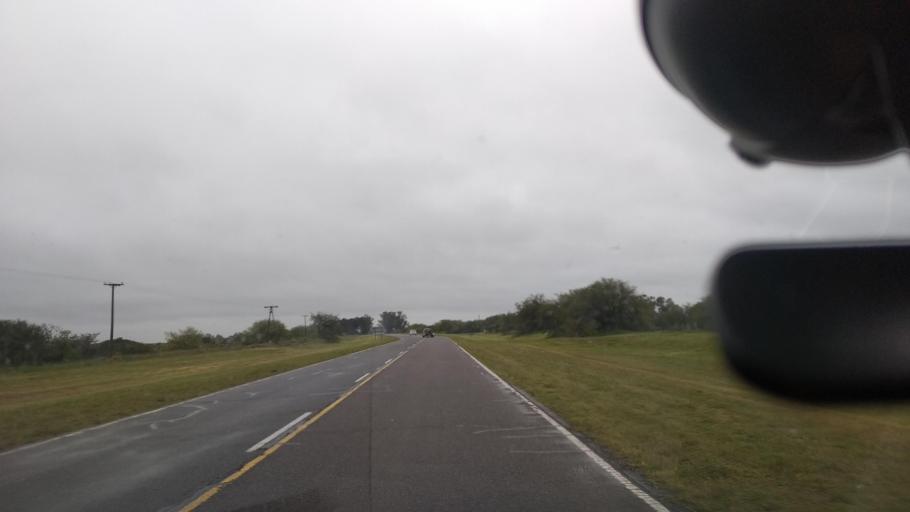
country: AR
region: Buenos Aires
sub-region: Partido de Castelli
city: Castelli
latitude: -36.0198
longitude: -57.4473
